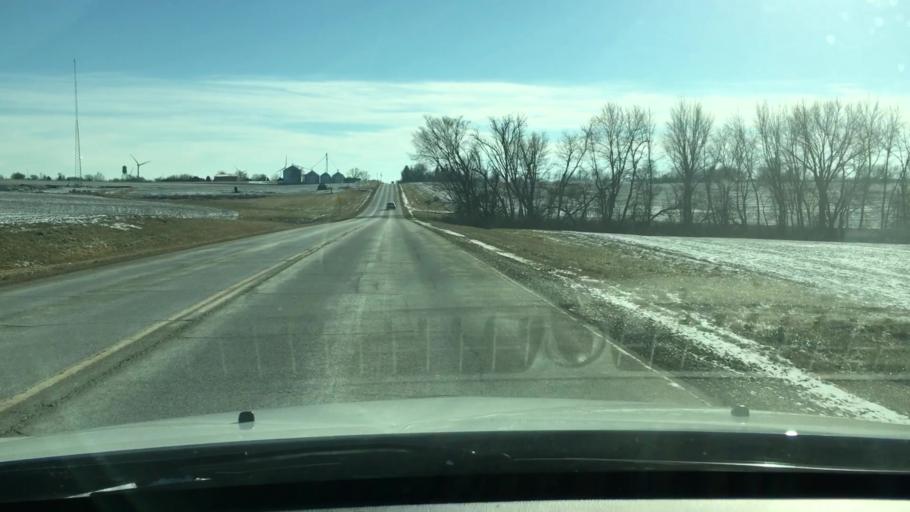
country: US
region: Illinois
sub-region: LaSalle County
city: Mendota
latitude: 41.7061
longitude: -89.0915
